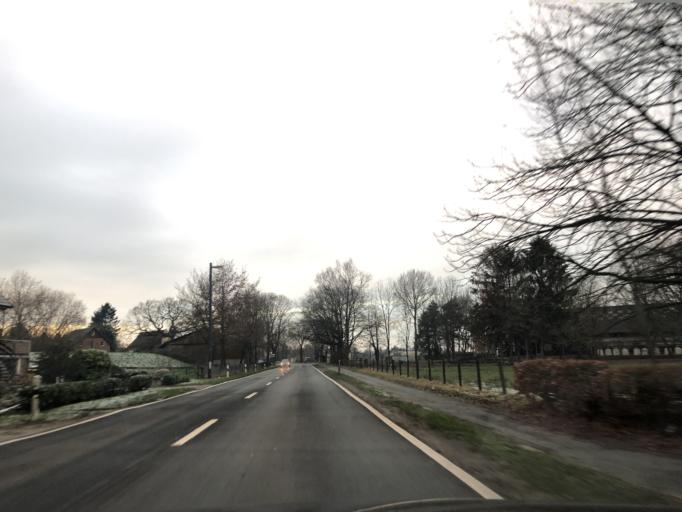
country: DE
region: Lower Saxony
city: Delmenhorst
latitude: 53.0888
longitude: 8.6742
